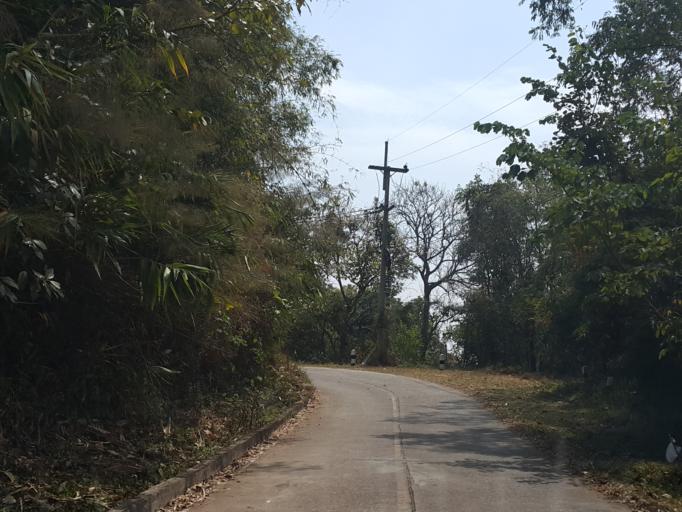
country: TH
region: Lampang
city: Mueang Pan
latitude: 18.8280
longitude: 99.3989
